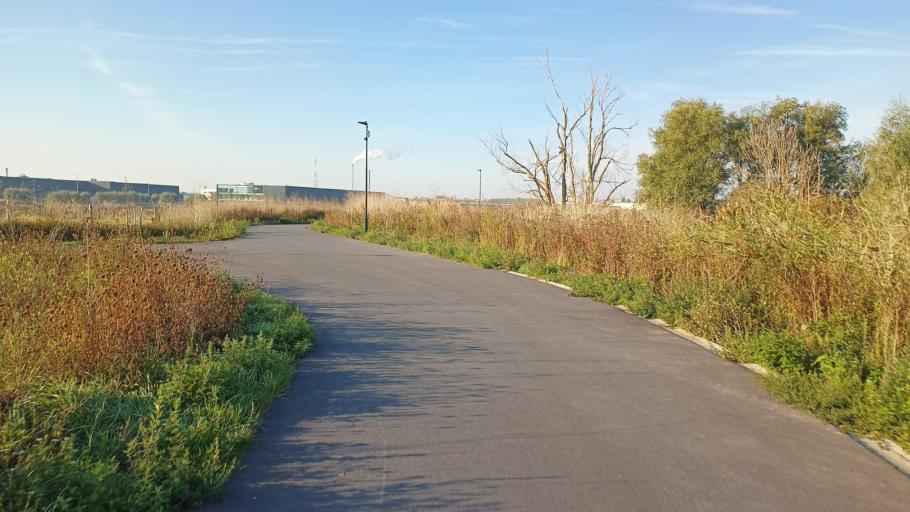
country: BE
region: Flanders
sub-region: Provincie West-Vlaanderen
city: Veurne
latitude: 51.0700
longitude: 2.6794
